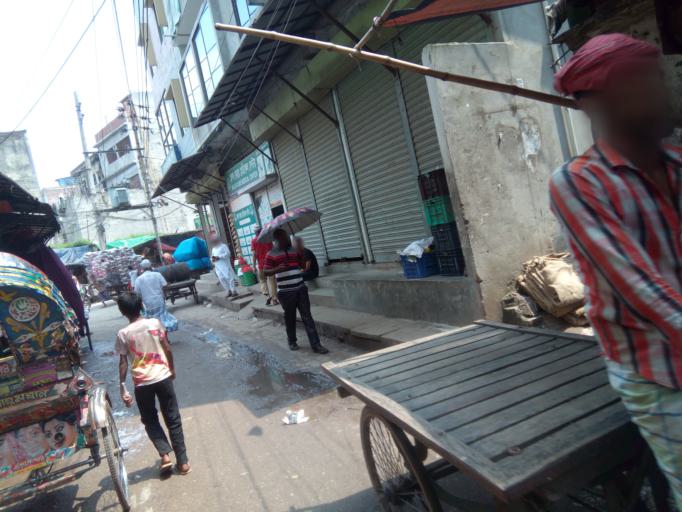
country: BD
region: Dhaka
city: Azimpur
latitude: 23.7162
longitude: 90.3851
